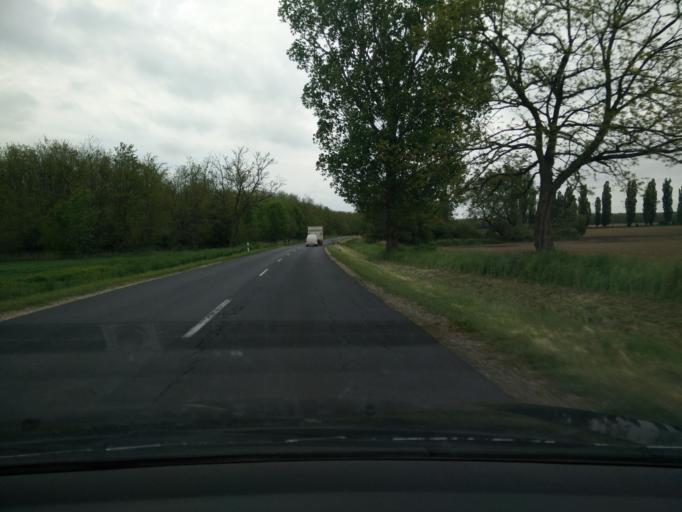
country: HU
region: Gyor-Moson-Sopron
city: Tet
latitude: 47.5366
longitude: 17.5345
